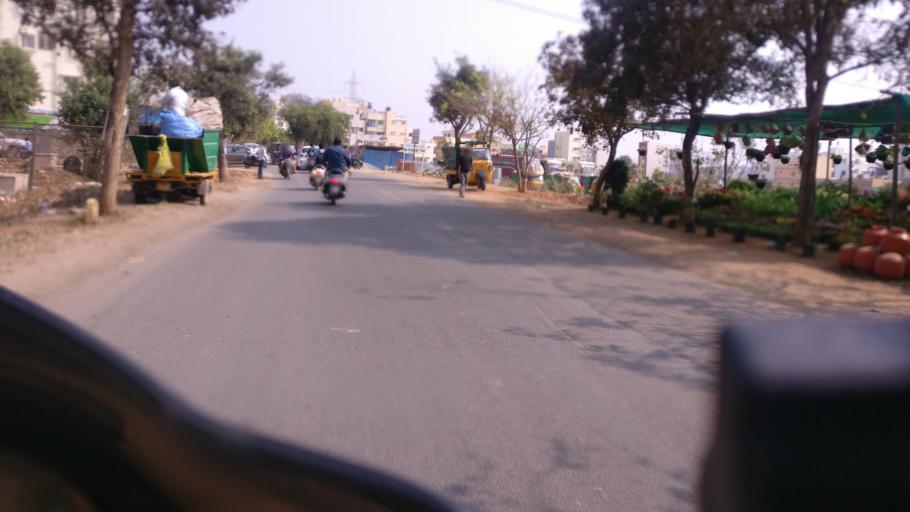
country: IN
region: Karnataka
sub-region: Bangalore Urban
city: Bangalore
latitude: 12.8753
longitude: 77.6545
